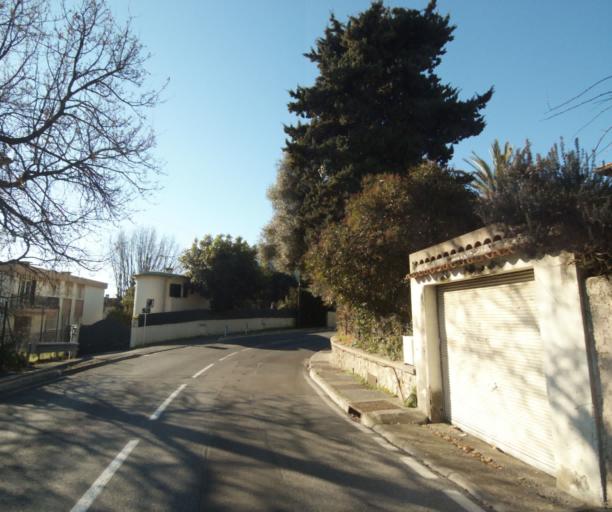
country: FR
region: Provence-Alpes-Cote d'Azur
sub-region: Departement des Alpes-Maritimes
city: Antibes
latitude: 43.5760
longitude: 7.1007
